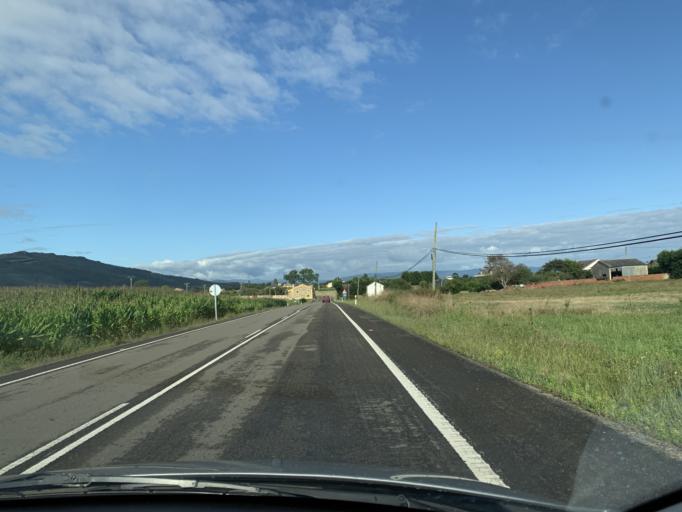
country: ES
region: Galicia
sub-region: Provincia de Lugo
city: Ribadeo
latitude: 43.5469
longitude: -7.1134
